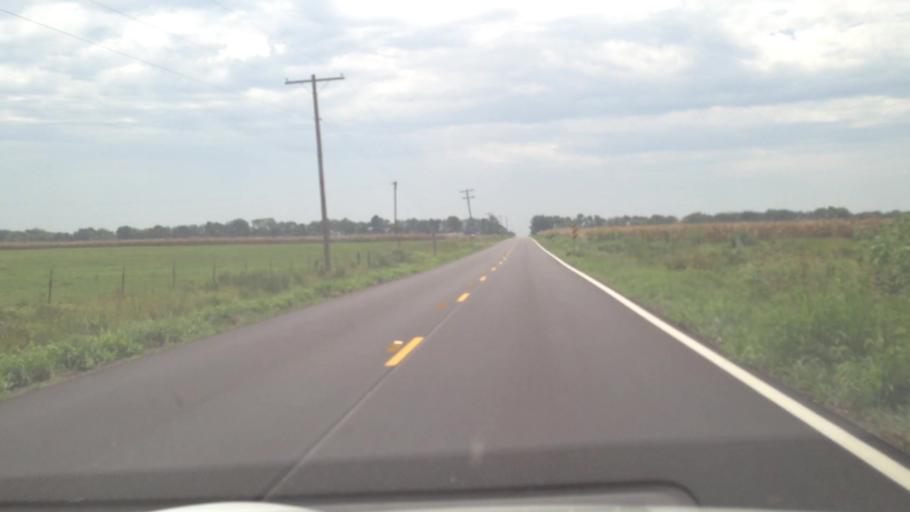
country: US
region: Kansas
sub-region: Crawford County
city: Girard
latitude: 37.6435
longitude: -94.9698
